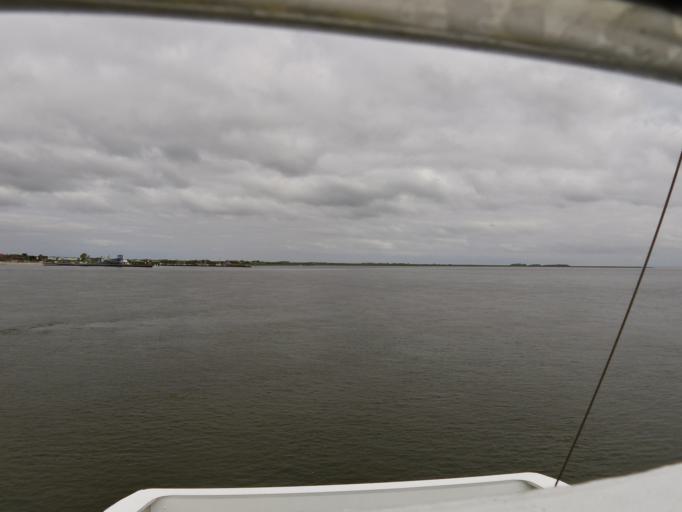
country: DE
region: Schleswig-Holstein
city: Wyk auf Fohr
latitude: 54.6878
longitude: 8.5863
